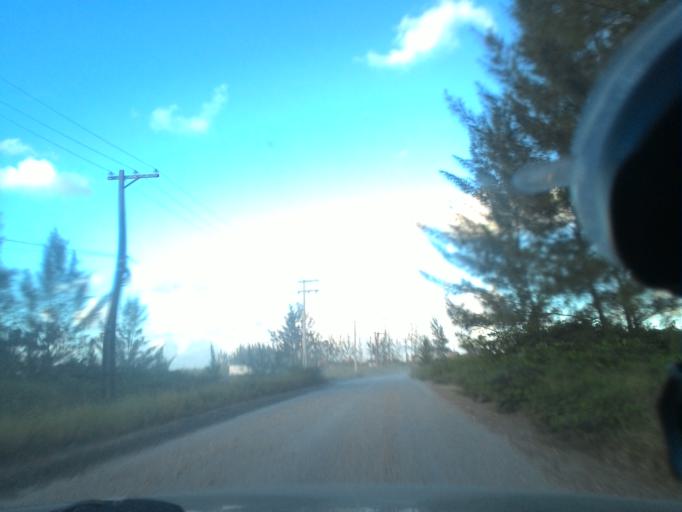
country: BR
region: Sao Paulo
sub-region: Iguape
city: Iguape
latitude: -24.8304
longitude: -47.6695
